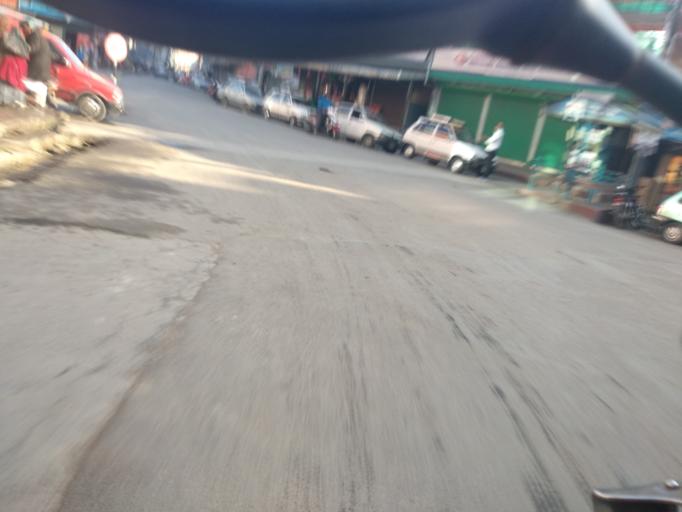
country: NP
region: Western Region
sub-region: Gandaki Zone
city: Pokhara
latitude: 28.2399
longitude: 83.9881
